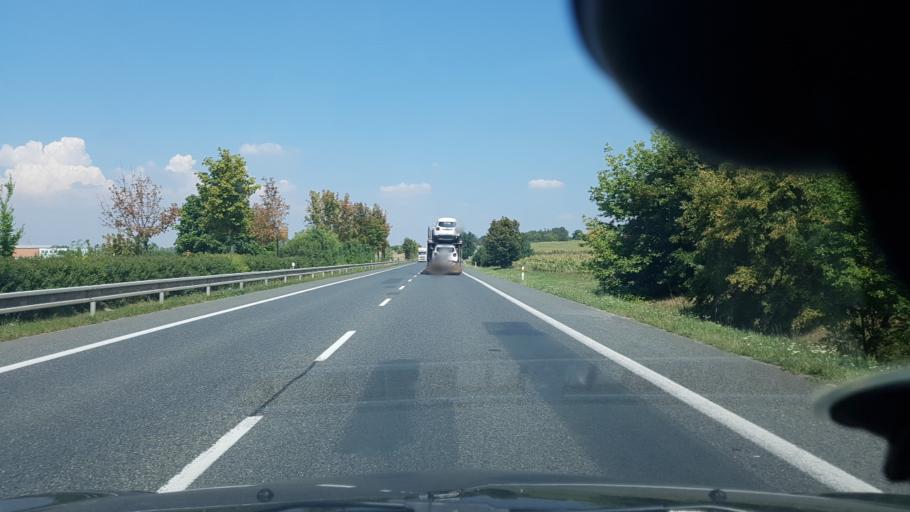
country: CZ
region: South Moravian
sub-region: Okres Breclav
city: Dolni Dunajovice
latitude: 48.8549
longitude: 16.6093
